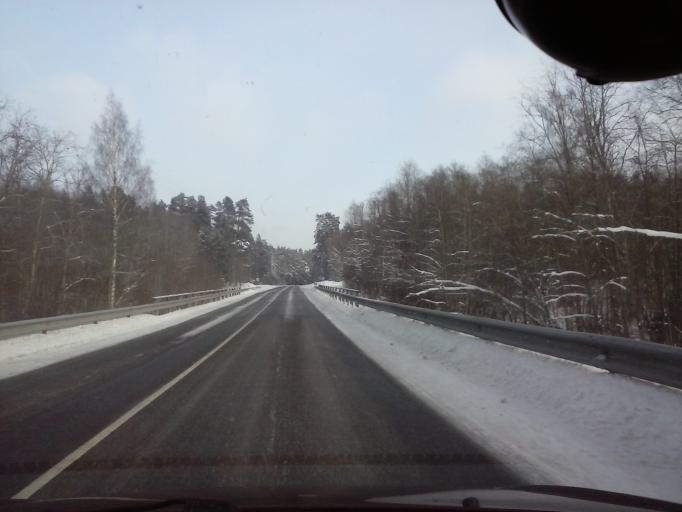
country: EE
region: Viljandimaa
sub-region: Moisakuela linn
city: Moisakula
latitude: 58.2451
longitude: 25.1405
